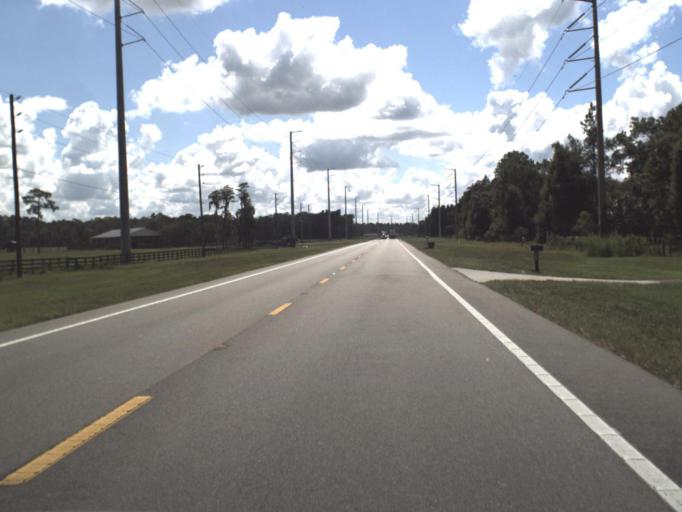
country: US
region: Florida
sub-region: Pasco County
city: Zephyrhills North
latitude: 28.2531
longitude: -82.0647
